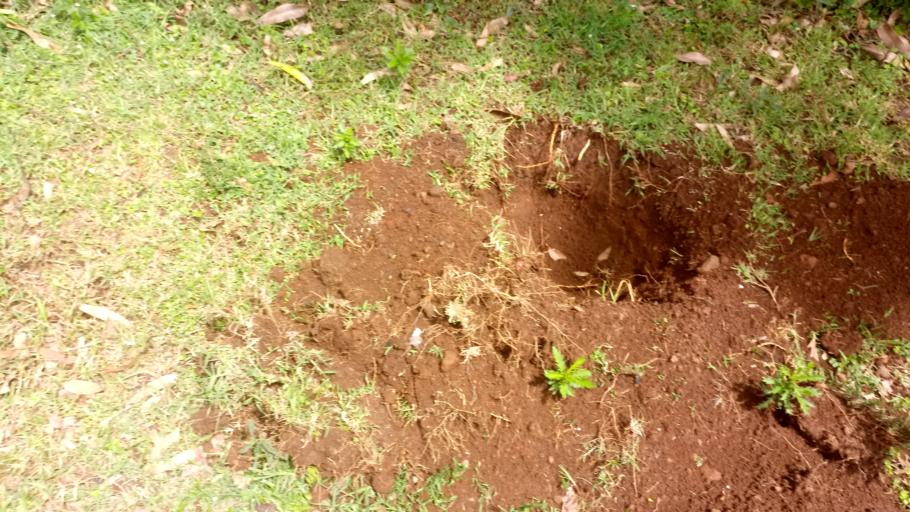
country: KE
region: Kirinyaga
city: Keruguya
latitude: -0.3971
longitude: 37.1598
